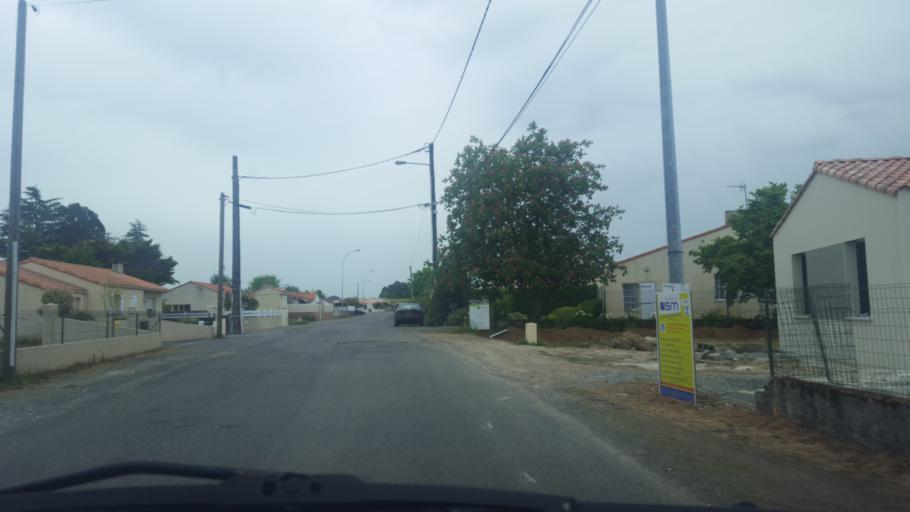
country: FR
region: Pays de la Loire
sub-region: Departement de la Loire-Atlantique
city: Saint-Philbert-de-Grand-Lieu
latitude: 47.0274
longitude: -1.6333
